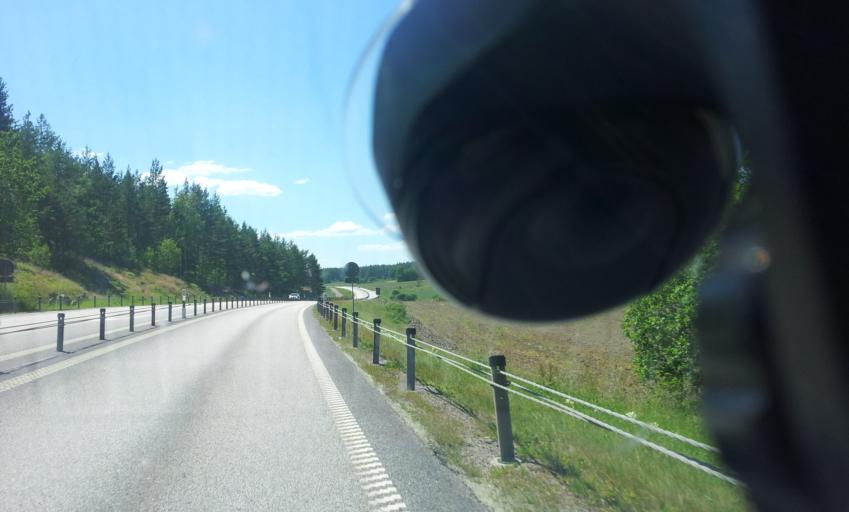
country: SE
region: Kalmar
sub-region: Vasterviks Kommun
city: Forserum
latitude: 57.9479
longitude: 16.4397
